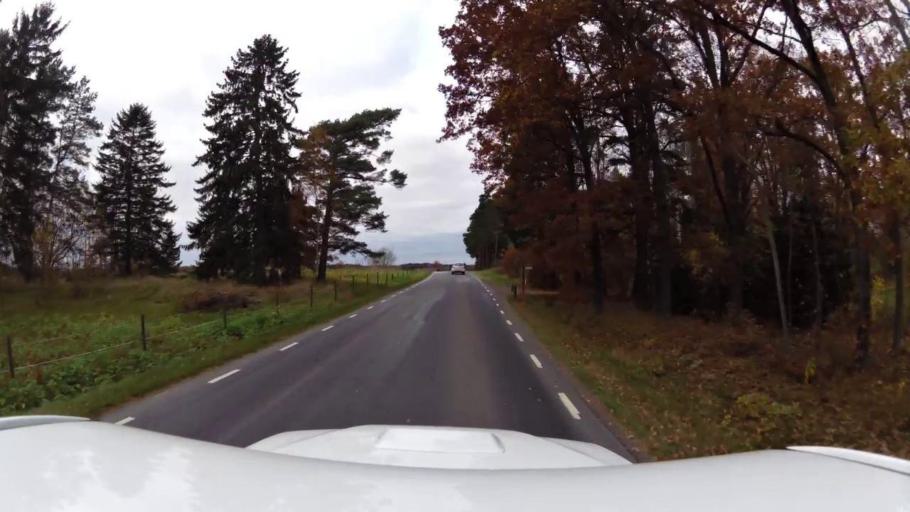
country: SE
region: OEstergoetland
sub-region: Linkopings Kommun
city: Linghem
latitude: 58.4156
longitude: 15.7412
